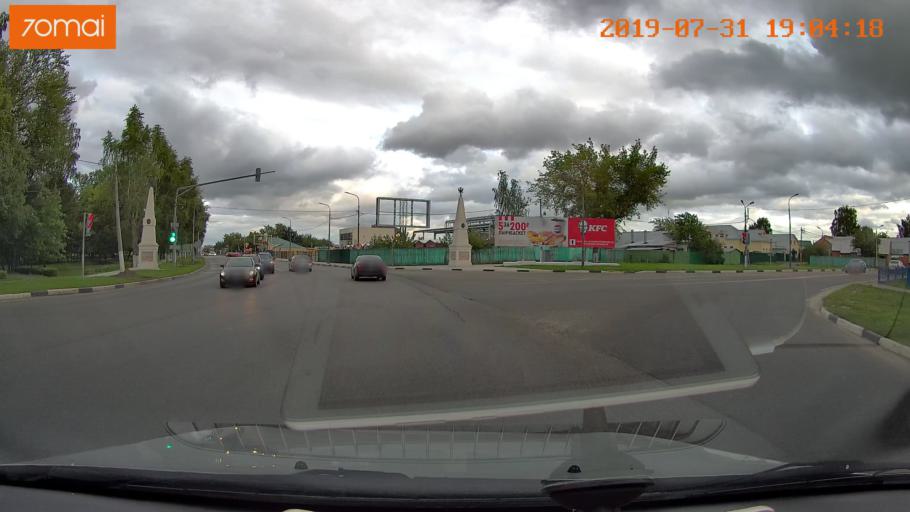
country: RU
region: Moskovskaya
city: Raduzhnyy
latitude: 55.1094
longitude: 38.7403
